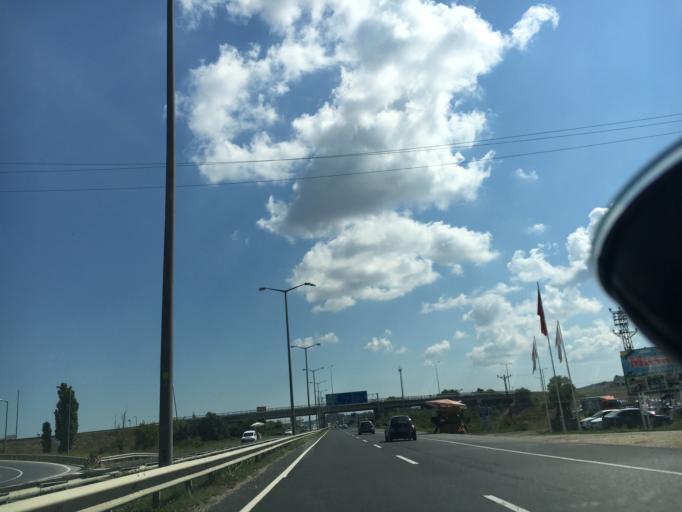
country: TR
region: Istanbul
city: Canta
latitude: 41.0670
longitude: 28.1034
